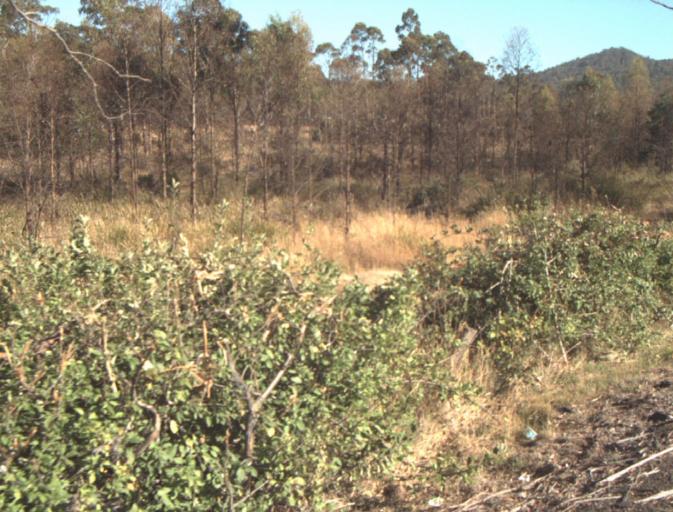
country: AU
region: Tasmania
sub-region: Launceston
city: Newstead
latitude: -41.3868
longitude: 147.2967
